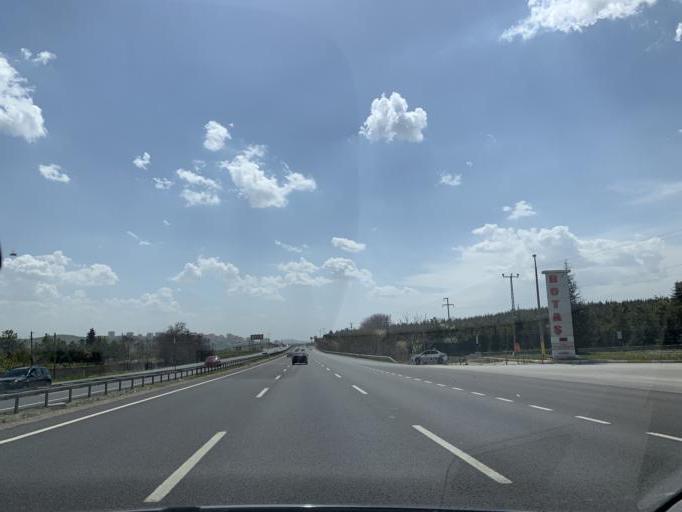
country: TR
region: Ankara
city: Etimesgut
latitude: 39.8450
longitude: 32.5942
